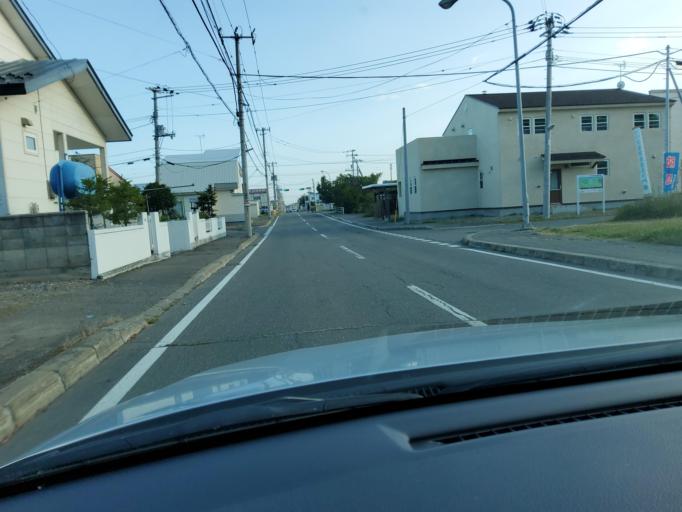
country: JP
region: Hokkaido
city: Obihiro
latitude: 42.9392
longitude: 143.1826
